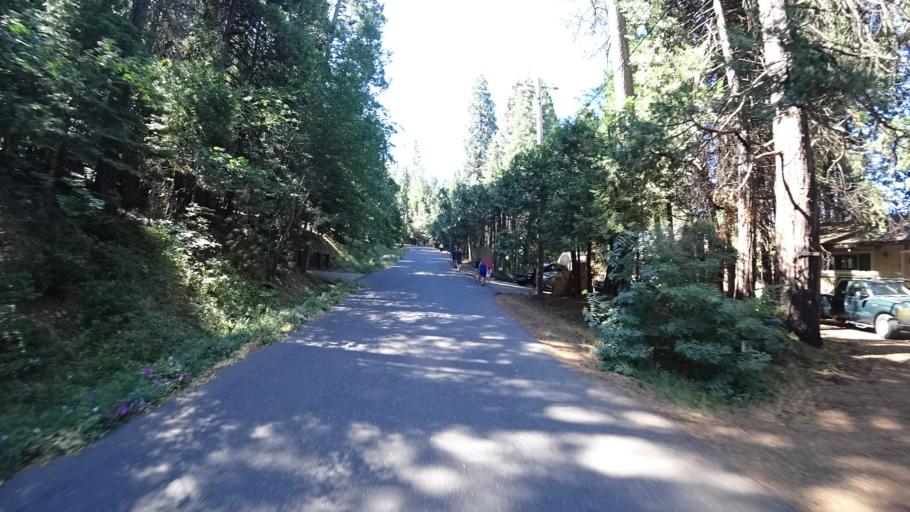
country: US
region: California
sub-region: Calaveras County
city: Arnold
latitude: 38.2534
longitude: -120.3281
